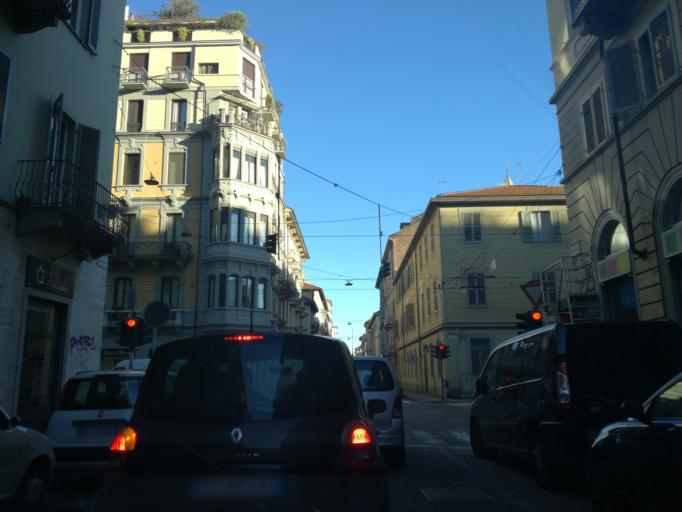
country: IT
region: Piedmont
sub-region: Provincia di Torino
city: Turin
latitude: 45.0778
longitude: 7.6649
